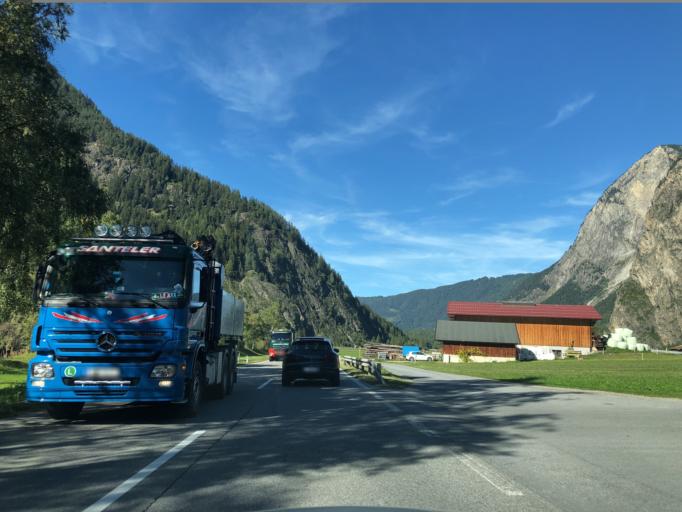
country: AT
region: Tyrol
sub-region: Politischer Bezirk Imst
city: Umhausen
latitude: 47.1529
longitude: 10.9124
